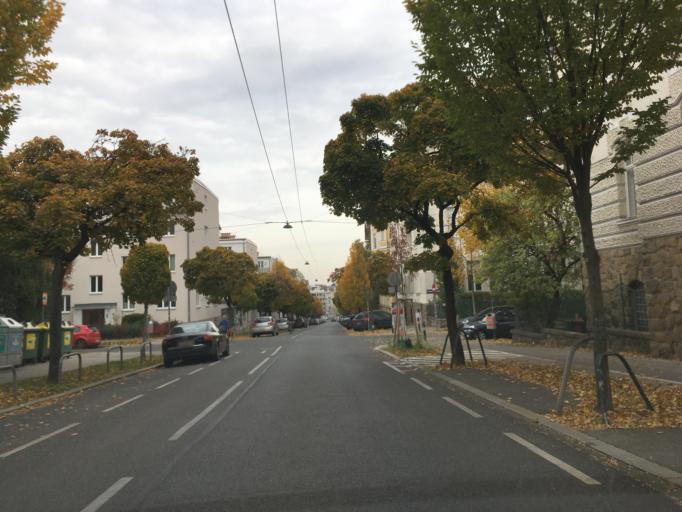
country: AT
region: Vienna
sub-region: Wien Stadt
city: Vienna
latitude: 48.2371
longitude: 16.3448
